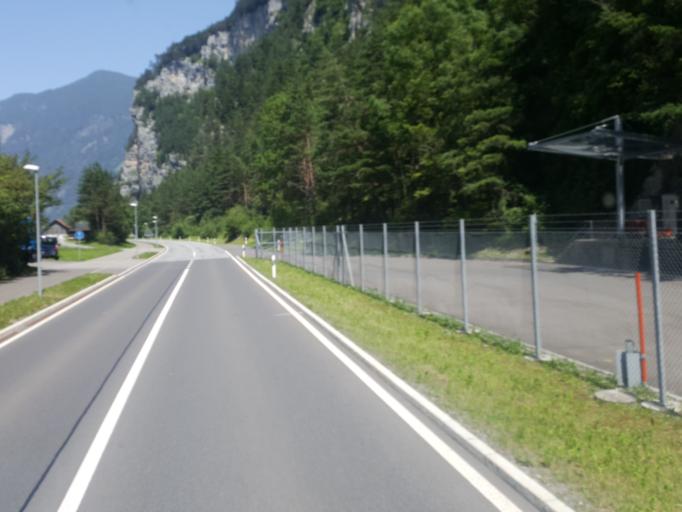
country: CH
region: Uri
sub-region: Uri
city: Schattdorf
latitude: 46.8440
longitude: 8.6450
